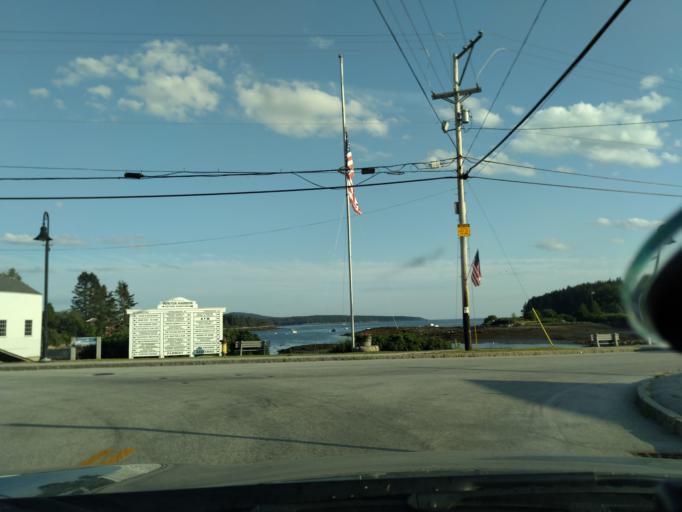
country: US
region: Maine
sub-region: Hancock County
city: Gouldsboro
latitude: 44.3950
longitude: -68.0842
